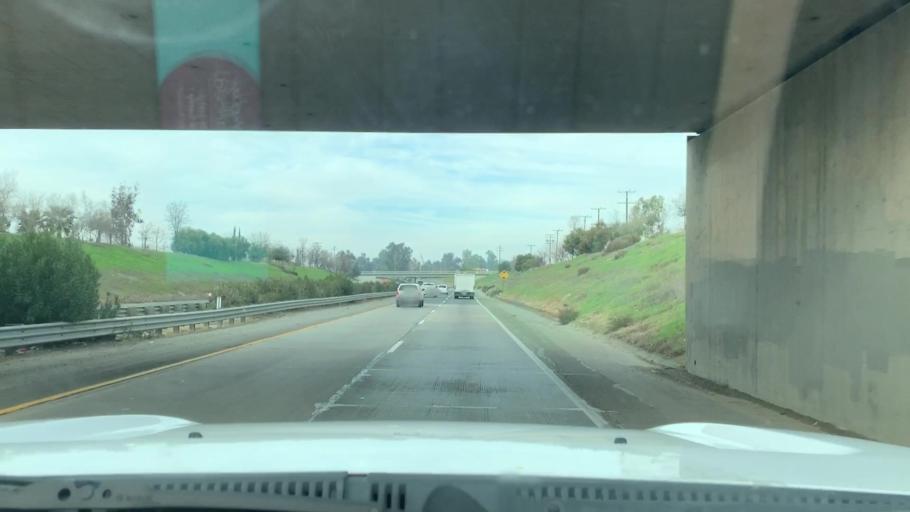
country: US
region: California
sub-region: Tulare County
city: Pixley
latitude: 35.9687
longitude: -119.2915
